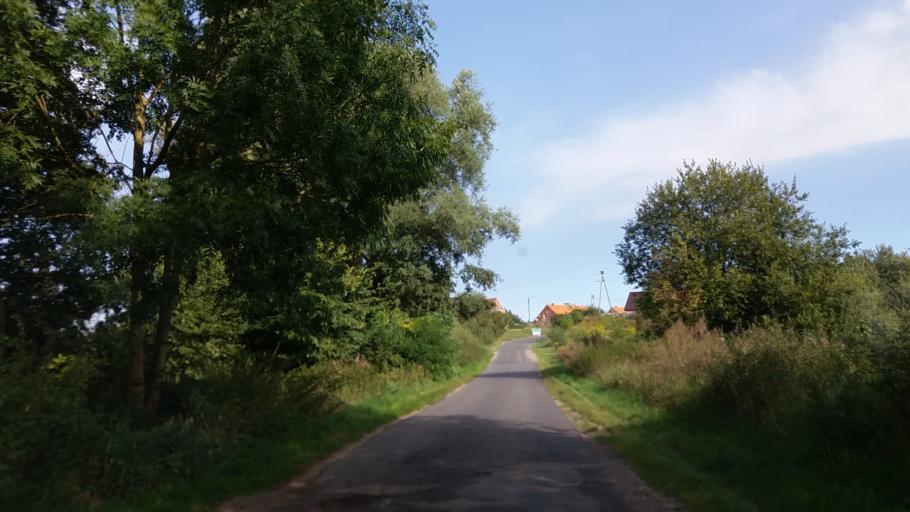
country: PL
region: West Pomeranian Voivodeship
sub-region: Powiat stargardzki
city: Suchan
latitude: 53.2252
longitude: 15.3417
